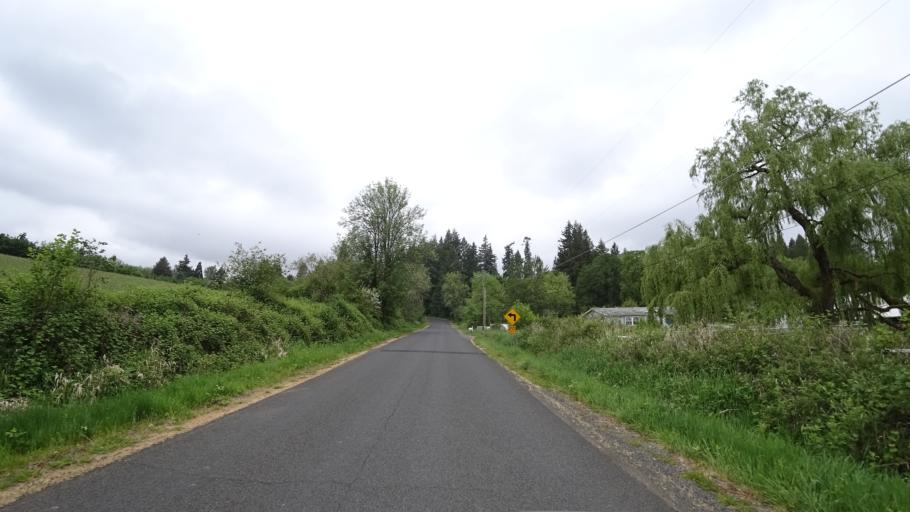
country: US
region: Oregon
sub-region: Washington County
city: Rockcreek
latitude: 45.5730
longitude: -122.8898
